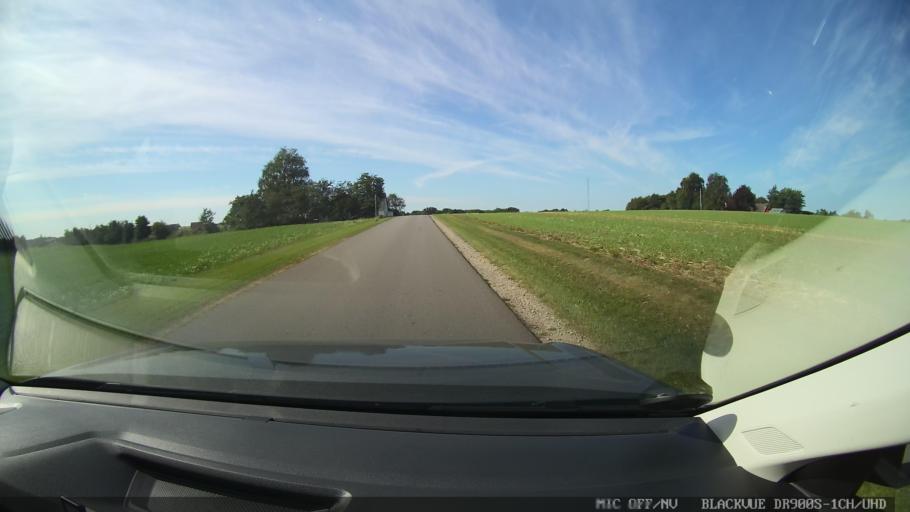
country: DK
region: North Denmark
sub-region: Mariagerfjord Kommune
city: Hobro
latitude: 56.5317
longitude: 9.7420
